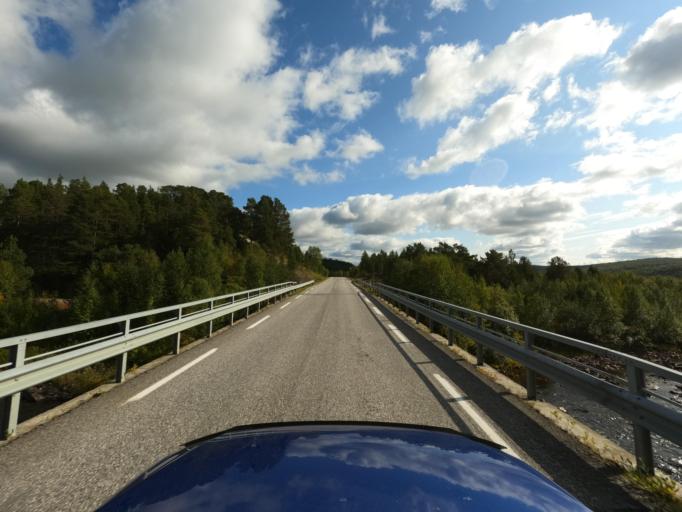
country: NO
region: Finnmark Fylke
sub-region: Karasjok
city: Karasjohka
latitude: 69.4437
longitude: 25.2282
